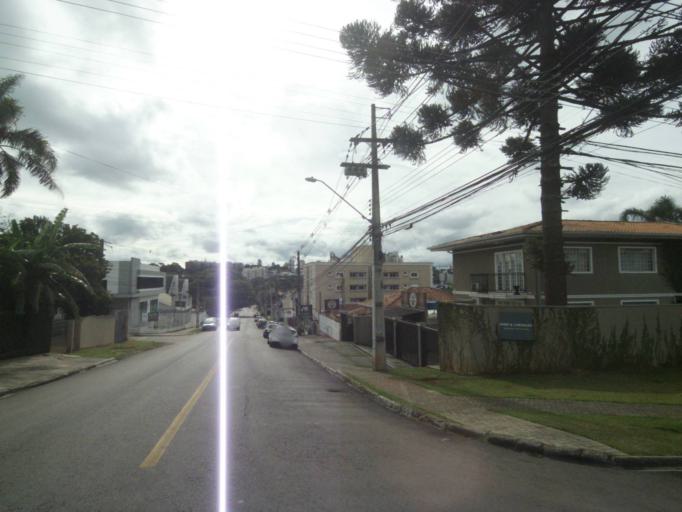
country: BR
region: Parana
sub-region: Curitiba
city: Curitiba
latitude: -25.4396
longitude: -49.3119
